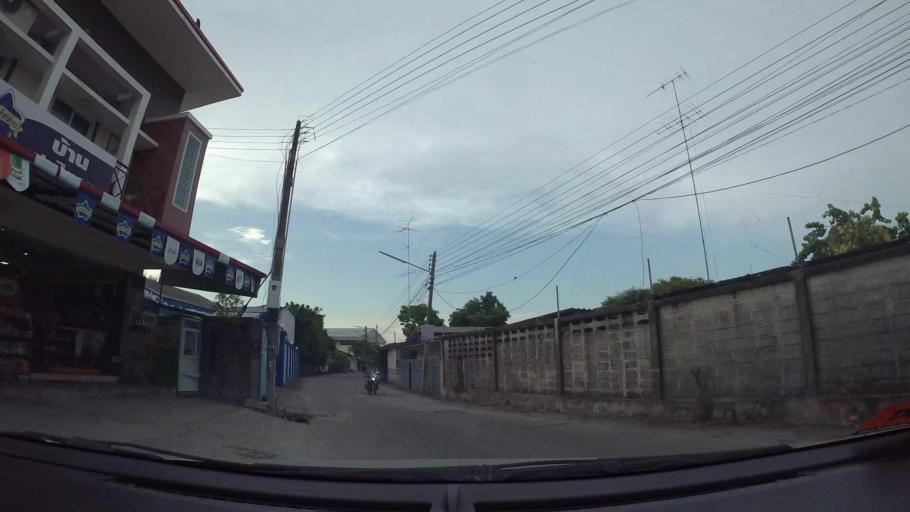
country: TH
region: Chon Buri
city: Chon Buri
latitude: 13.3398
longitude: 100.9876
